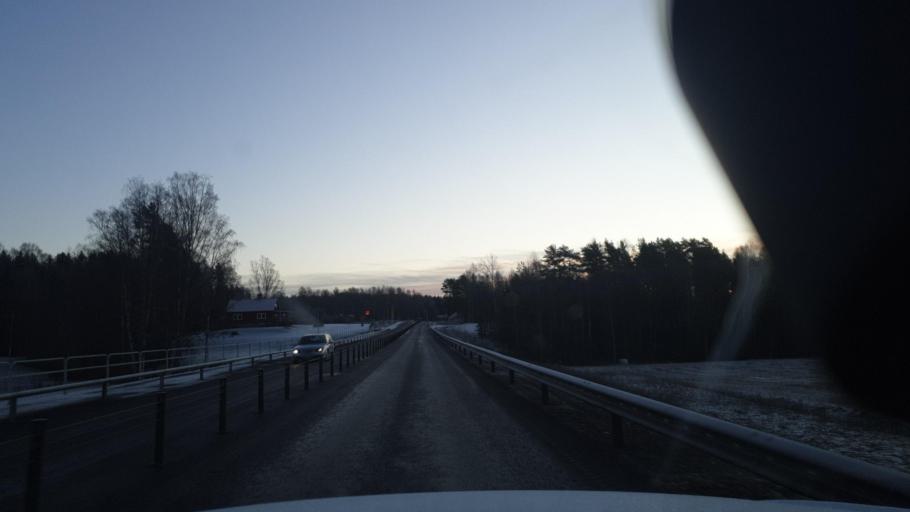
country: SE
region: Vaermland
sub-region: Arvika Kommun
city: Arvika
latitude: 59.7085
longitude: 12.5620
